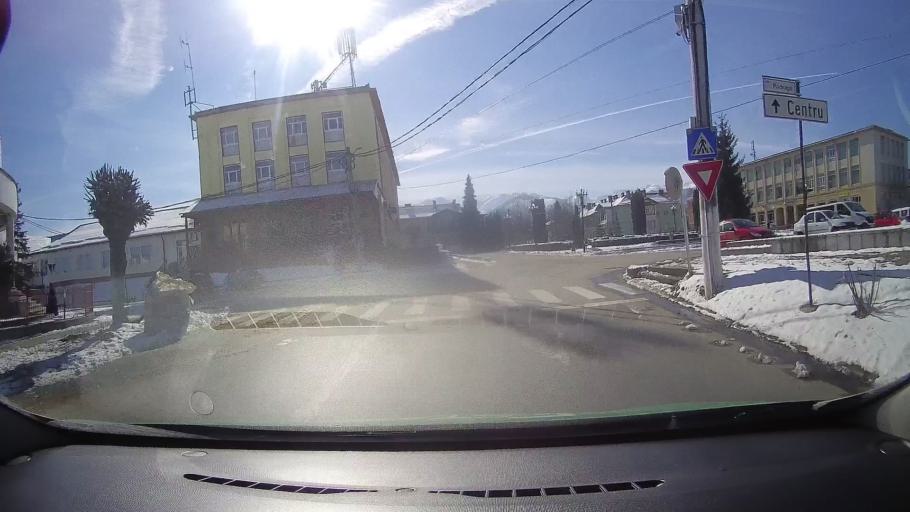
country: RO
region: Brasov
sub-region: Oras Victoria
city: Victoria
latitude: 45.7304
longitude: 24.7015
